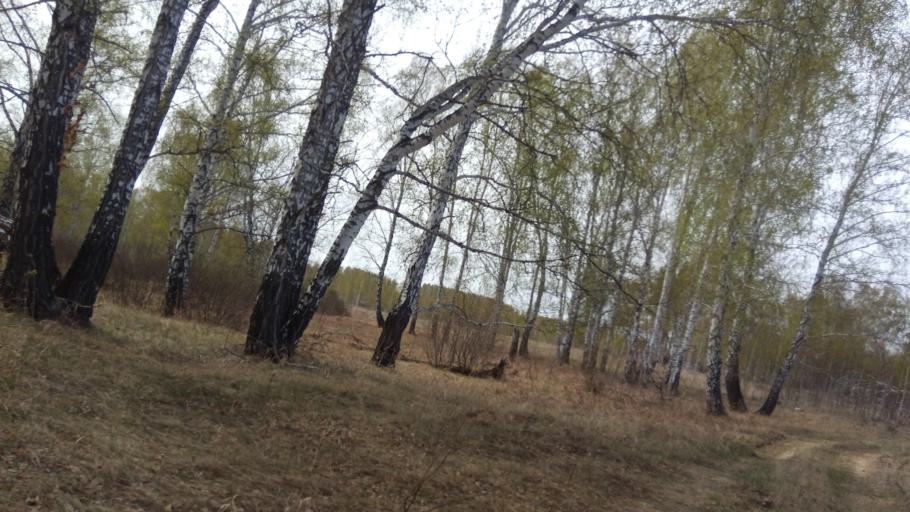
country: RU
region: Chelyabinsk
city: Timiryazevskiy
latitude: 55.0087
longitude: 60.8598
